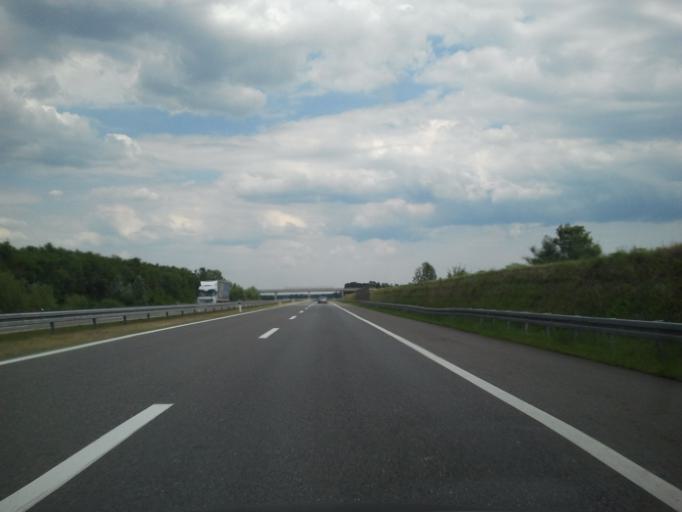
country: HR
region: Vukovarsko-Srijemska
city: Stitar
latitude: 45.1106
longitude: 18.6487
